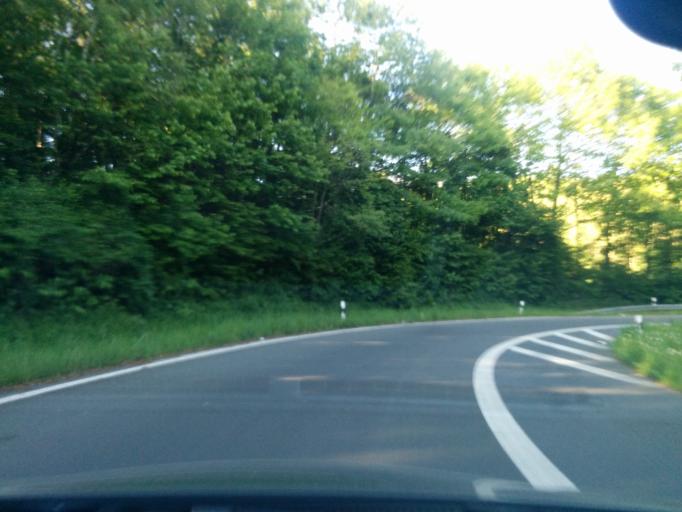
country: DE
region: North Rhine-Westphalia
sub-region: Regierungsbezirk Koln
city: Konigswinter
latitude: 50.7259
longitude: 7.1627
